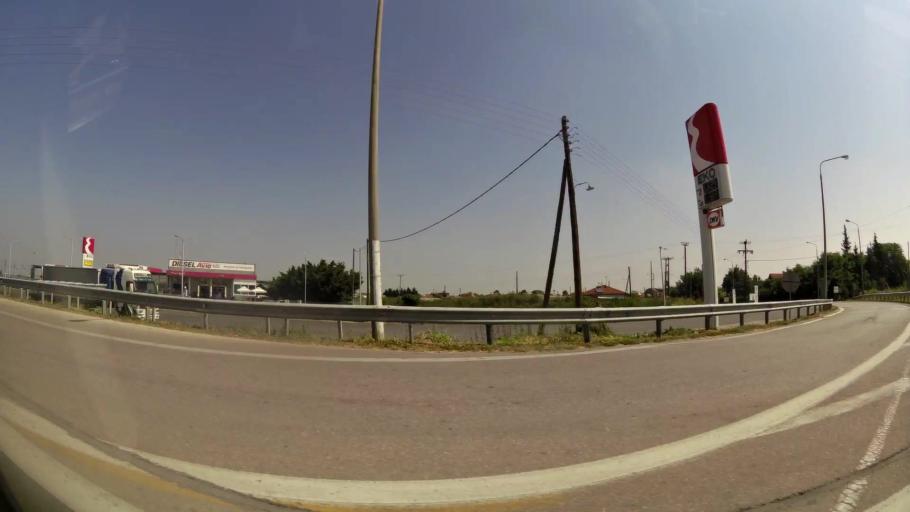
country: GR
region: Central Macedonia
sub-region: Nomos Imathias
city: Kleidi
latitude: 40.5594
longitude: 22.5872
